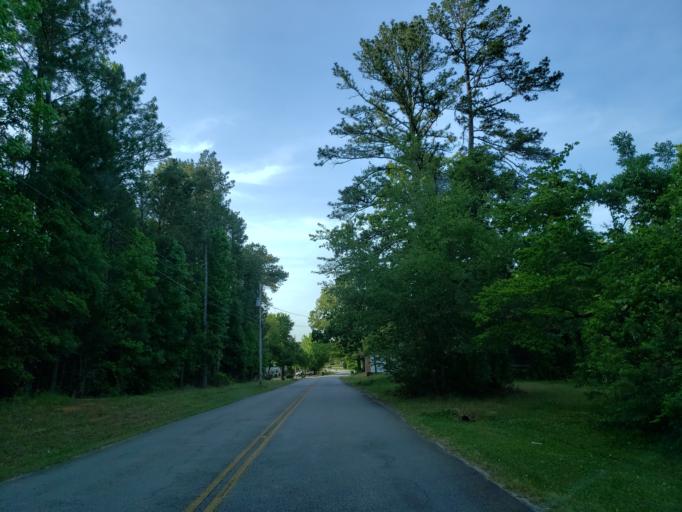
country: US
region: Georgia
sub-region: Carroll County
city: Mount Zion
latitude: 33.6368
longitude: -85.1874
